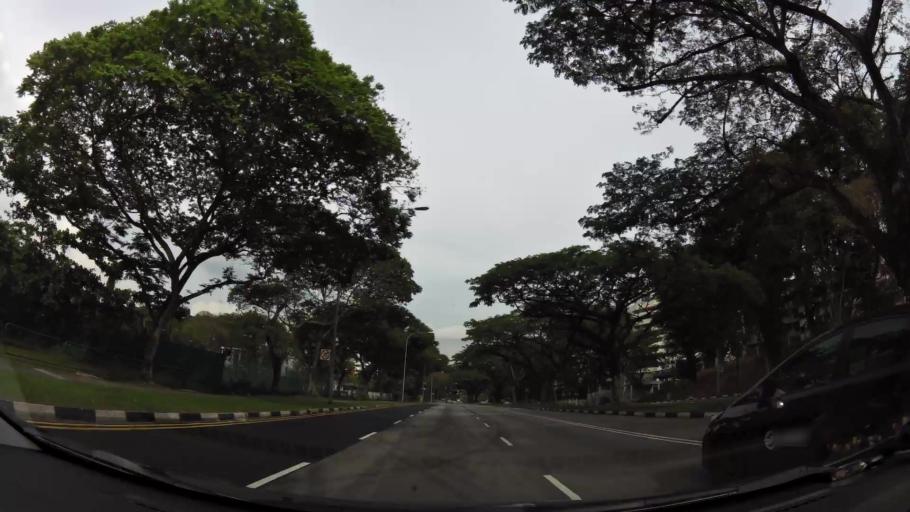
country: SG
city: Singapore
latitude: 1.3209
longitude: 103.7774
